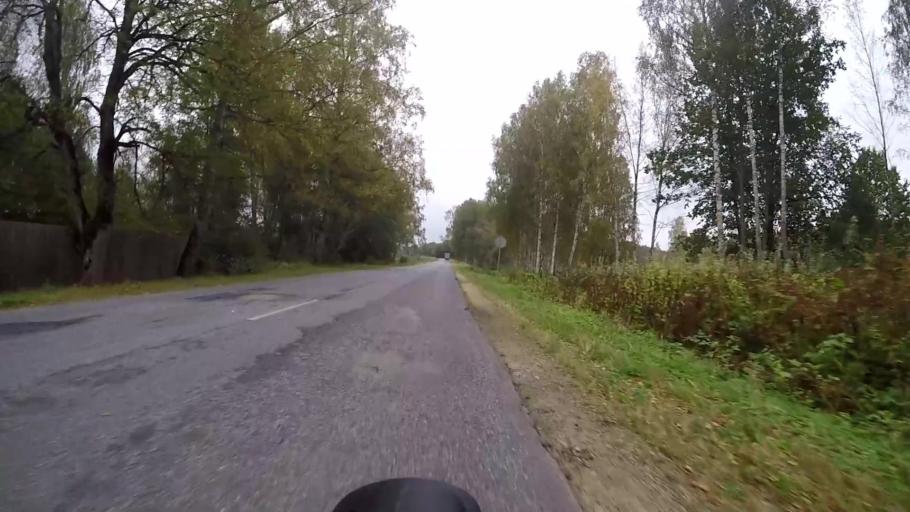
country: LV
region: Krimulda
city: Ragana
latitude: 57.2544
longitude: 24.6498
